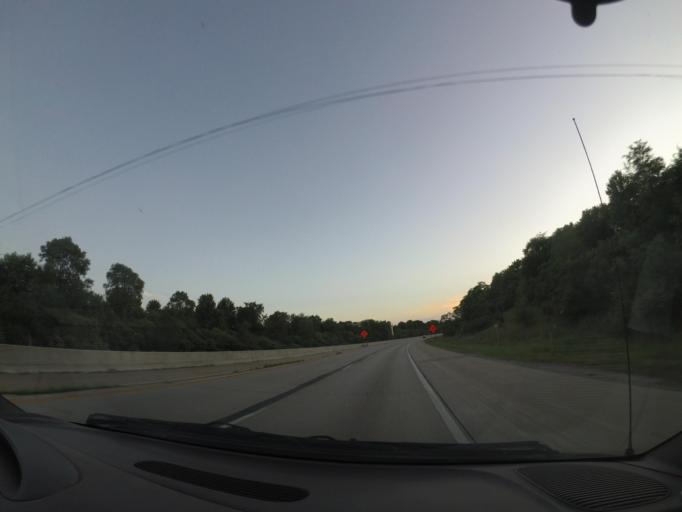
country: US
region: Indiana
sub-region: Elkhart County
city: Dunlap
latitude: 41.6592
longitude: -85.9048
